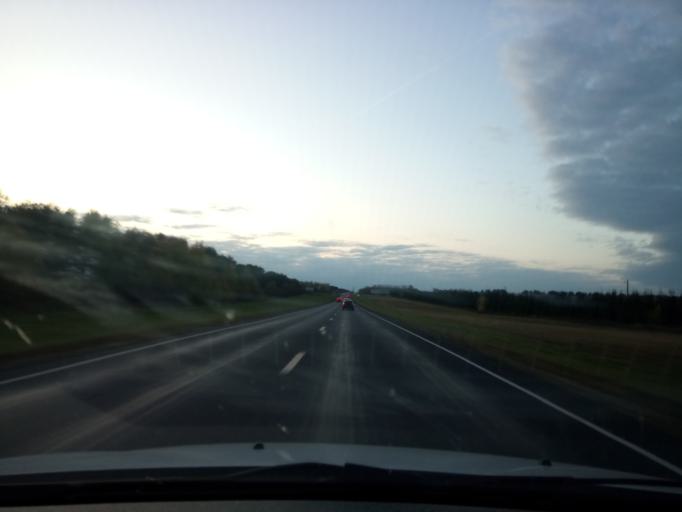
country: RU
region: Nizjnij Novgorod
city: Bol'shoye Murashkino
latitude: 55.8971
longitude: 44.7277
